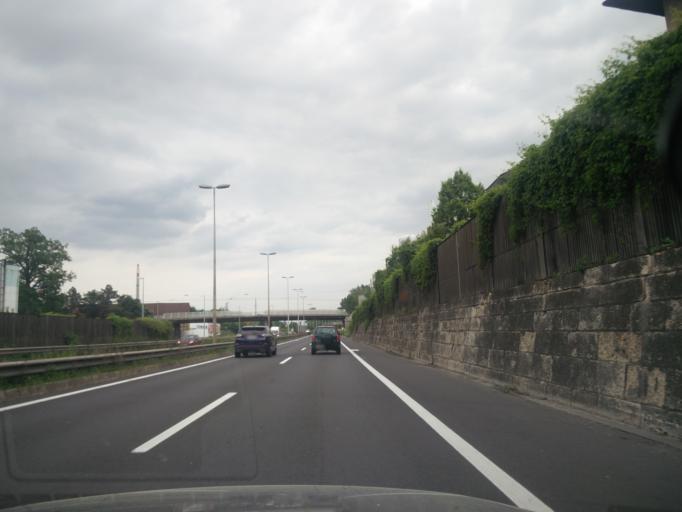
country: AT
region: Upper Austria
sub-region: Linz Stadt
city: Linz
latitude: 48.3102
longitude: 14.3110
